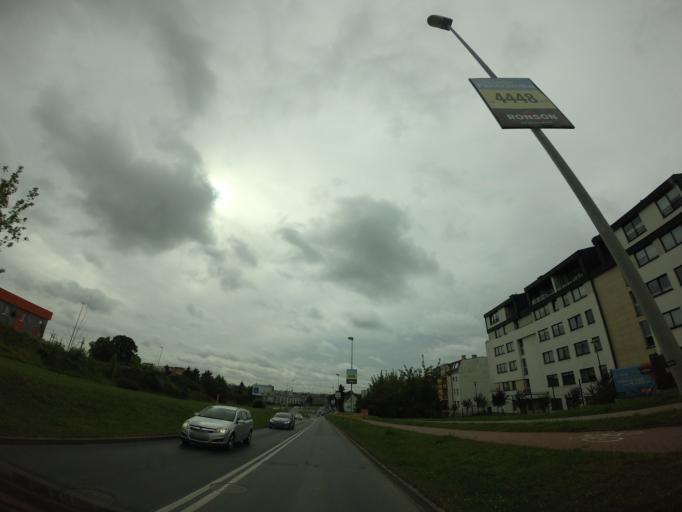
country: PL
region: West Pomeranian Voivodeship
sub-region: Szczecin
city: Szczecin
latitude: 53.4578
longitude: 14.5431
